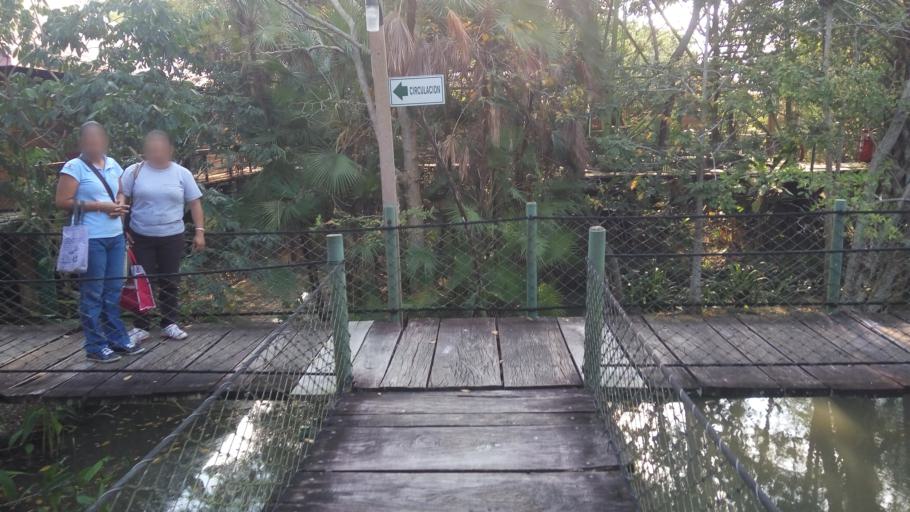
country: MX
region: Tabasco
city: Frontera
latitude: 18.4057
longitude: -92.6476
